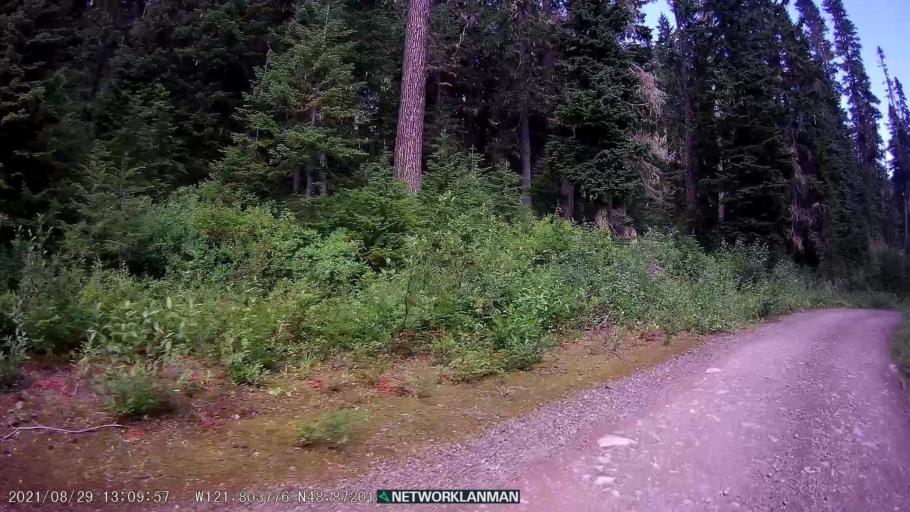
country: CA
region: British Columbia
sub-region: Fraser Valley Regional District
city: Chilliwack
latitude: 48.8716
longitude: -121.8047
